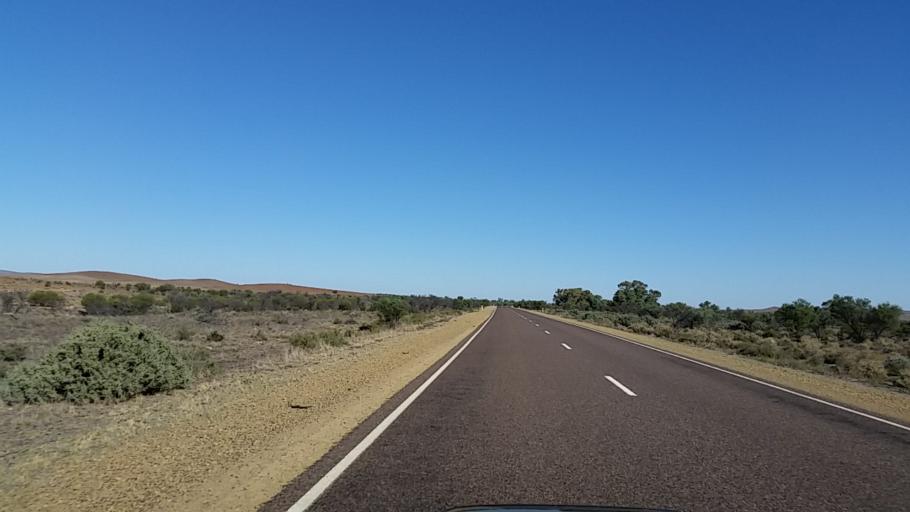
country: AU
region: South Australia
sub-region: Flinders Ranges
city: Quorn
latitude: -32.3664
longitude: 138.4973
